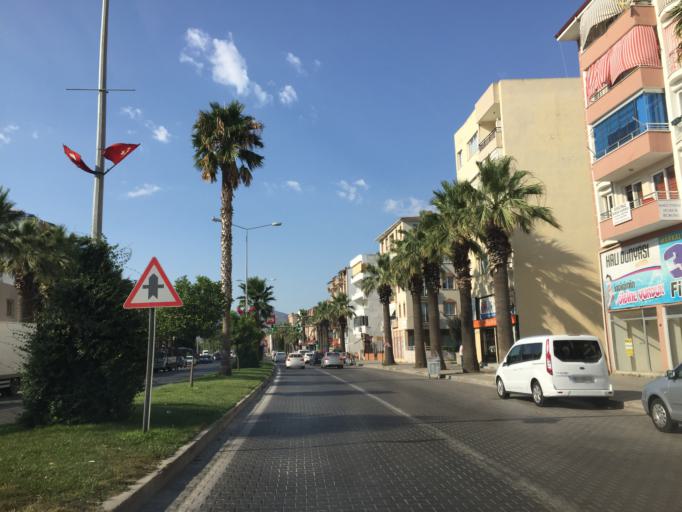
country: TR
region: Izmir
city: Selcuk
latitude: 37.9528
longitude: 27.3710
